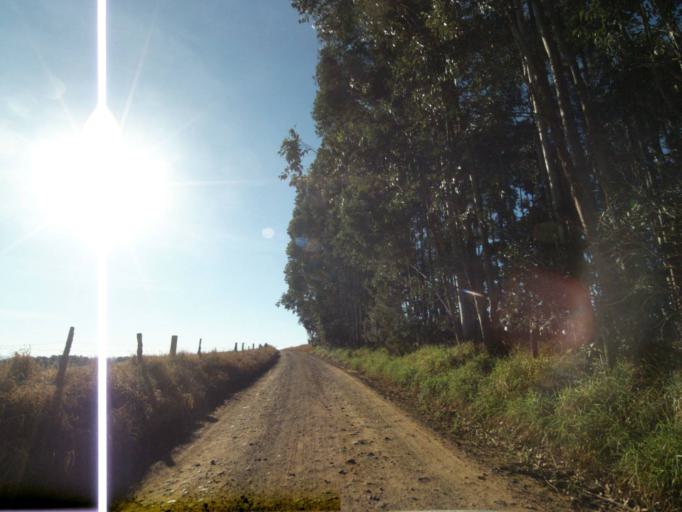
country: BR
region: Parana
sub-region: Tibagi
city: Tibagi
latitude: -24.5388
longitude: -50.6255
